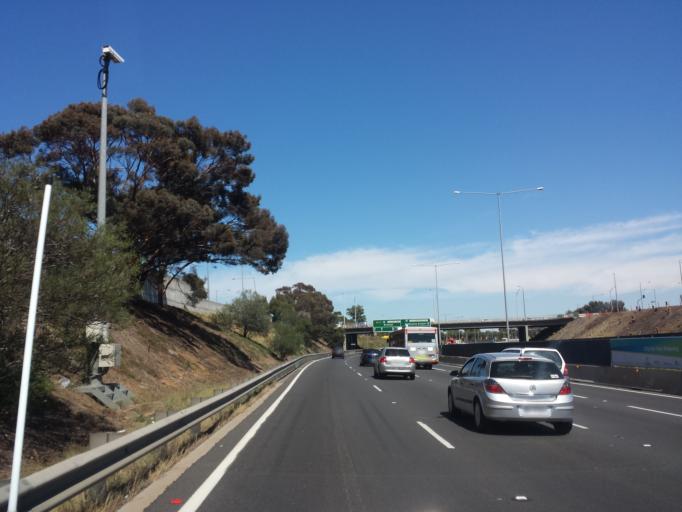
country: AU
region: Victoria
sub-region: Moonee Valley
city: Essendon North
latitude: -37.7351
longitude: 144.9067
